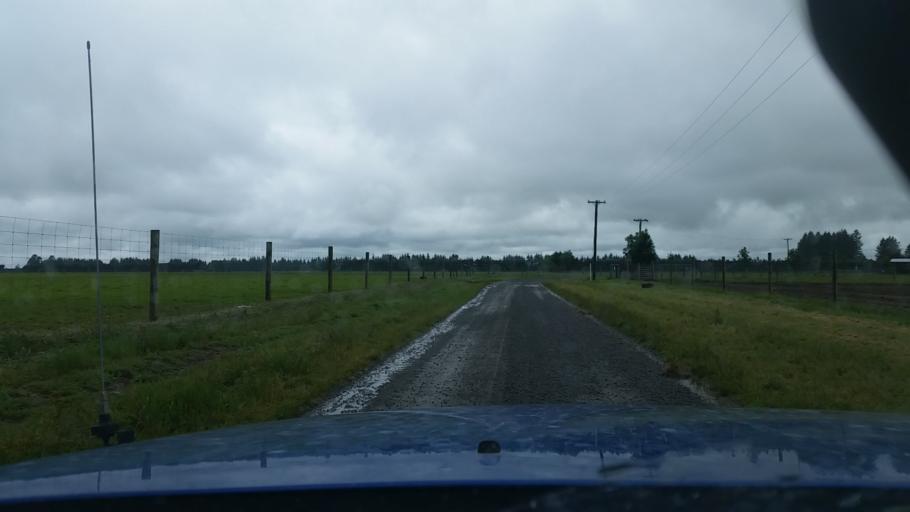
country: NZ
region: Canterbury
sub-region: Ashburton District
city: Methven
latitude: -43.6045
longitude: 171.5031
